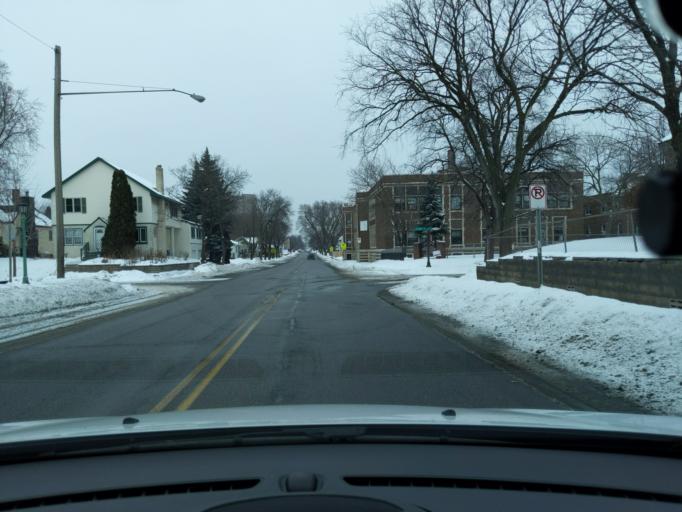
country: US
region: Minnesota
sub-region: Ramsey County
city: Falcon Heights
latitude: 44.9600
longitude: -93.1568
